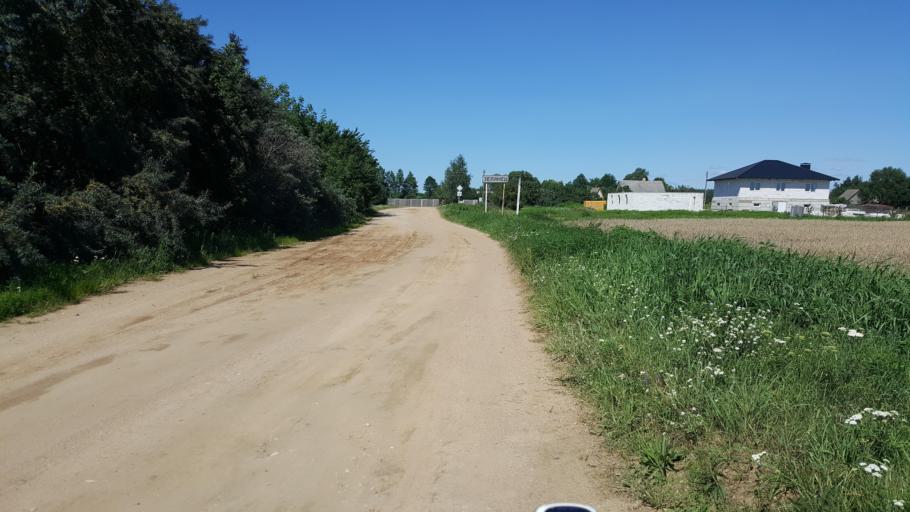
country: BY
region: Brest
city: Charnawchytsy
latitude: 52.2091
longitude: 23.7903
